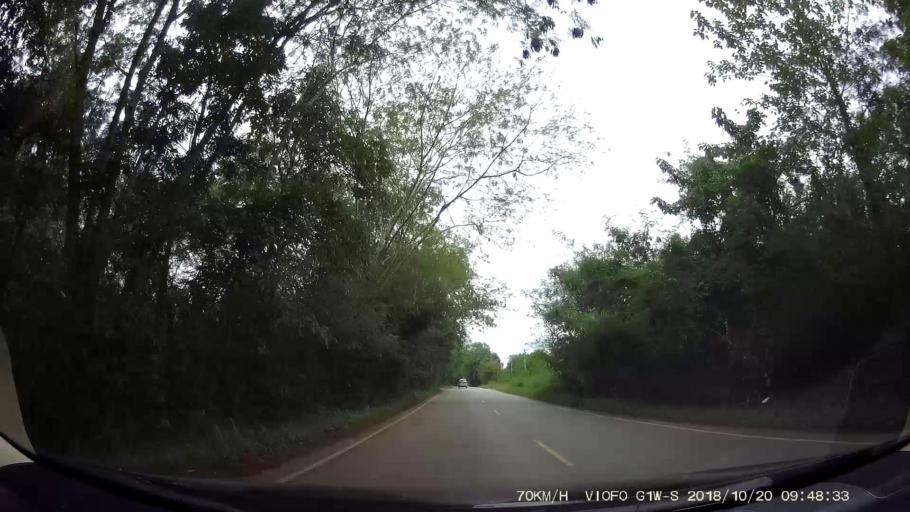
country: TH
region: Chaiyaphum
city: Khon San
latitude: 16.5121
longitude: 101.9112
